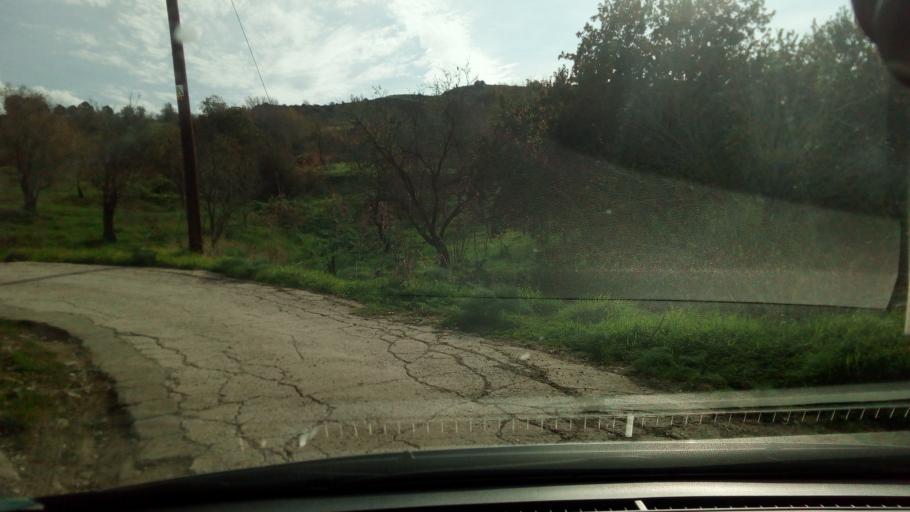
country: CY
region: Pafos
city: Mesogi
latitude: 34.7938
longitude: 32.4780
